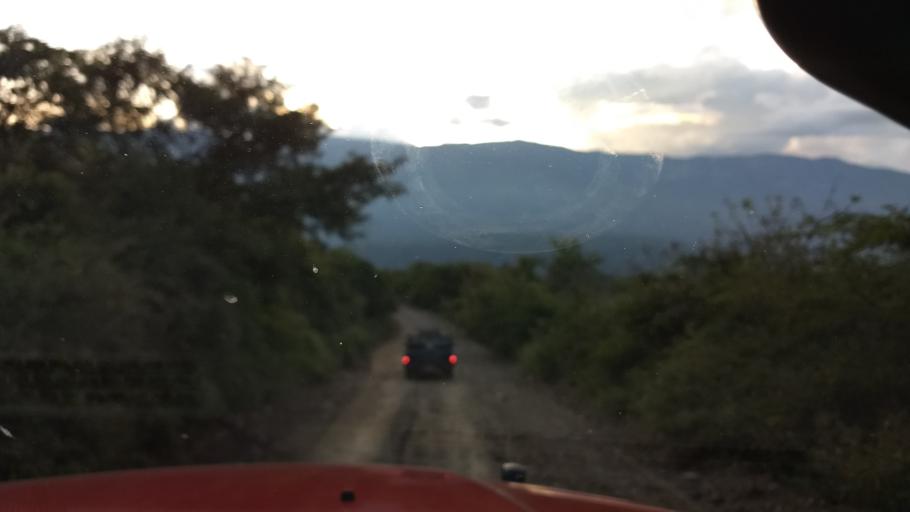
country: MX
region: Colima
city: Suchitlan
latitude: 19.4798
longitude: -103.8012
